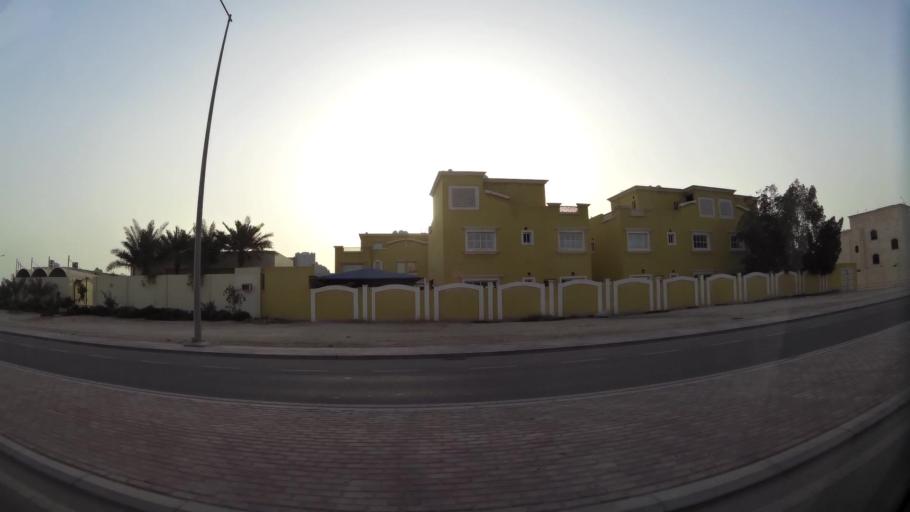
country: QA
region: Baladiyat ar Rayyan
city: Ar Rayyan
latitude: 25.2464
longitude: 51.4438
